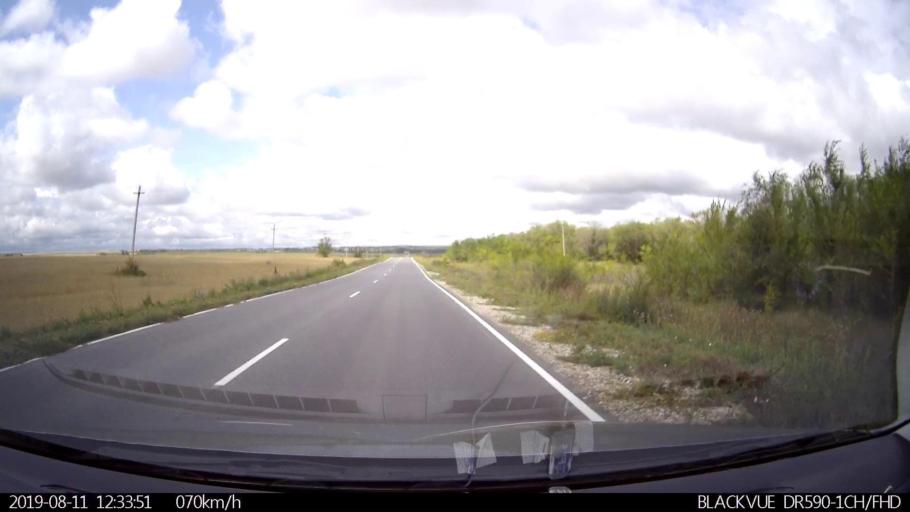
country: RU
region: Ulyanovsk
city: Ignatovka
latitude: 53.8126
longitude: 47.8505
